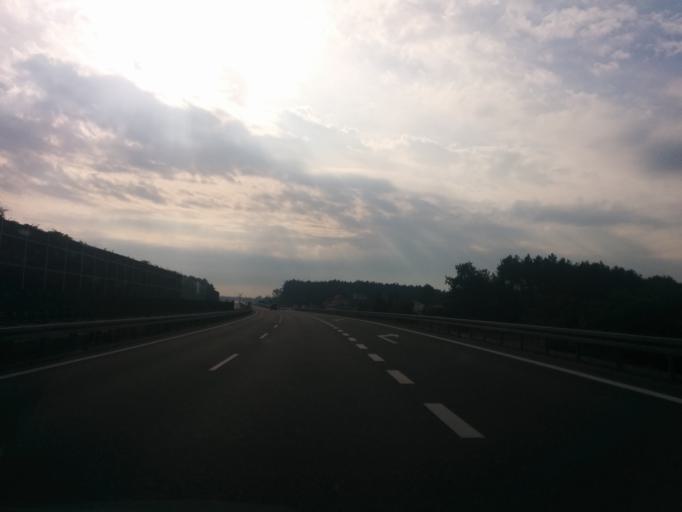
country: PL
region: Masovian Voivodeship
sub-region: Powiat bialobrzeski
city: Stara Blotnica
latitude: 51.5793
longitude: 21.0038
